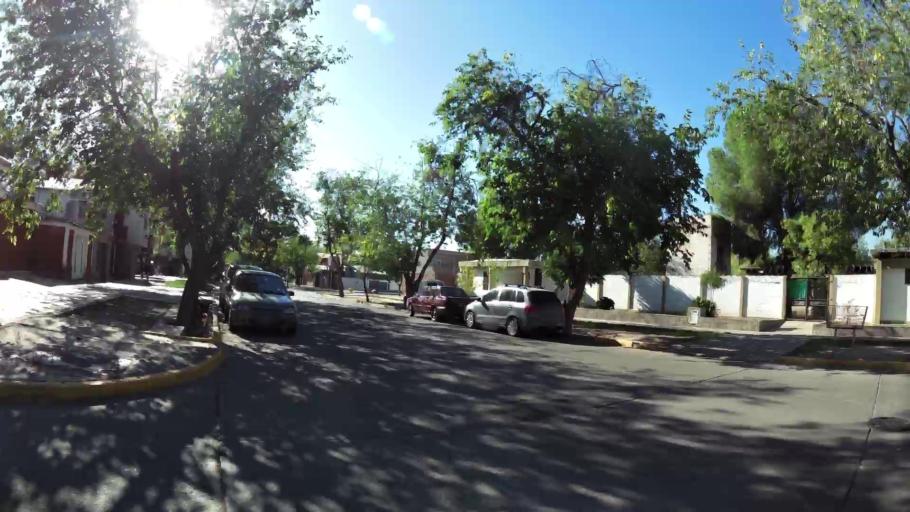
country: AR
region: Mendoza
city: Las Heras
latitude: -32.8676
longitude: -68.8488
